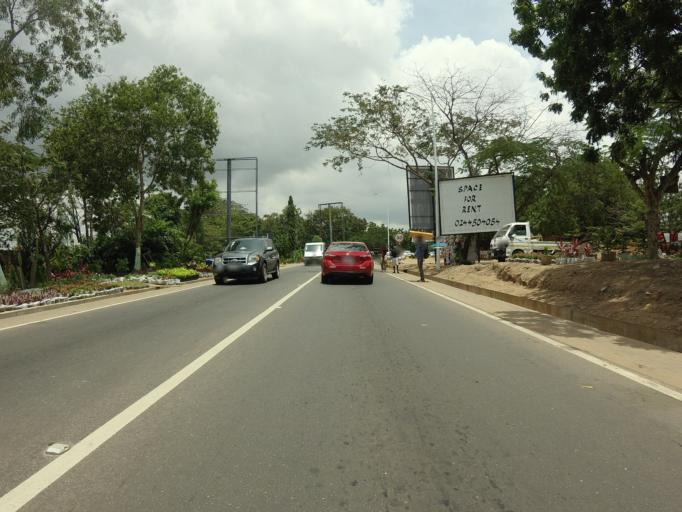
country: GH
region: Greater Accra
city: Medina Estates
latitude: 5.6267
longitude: -0.1587
